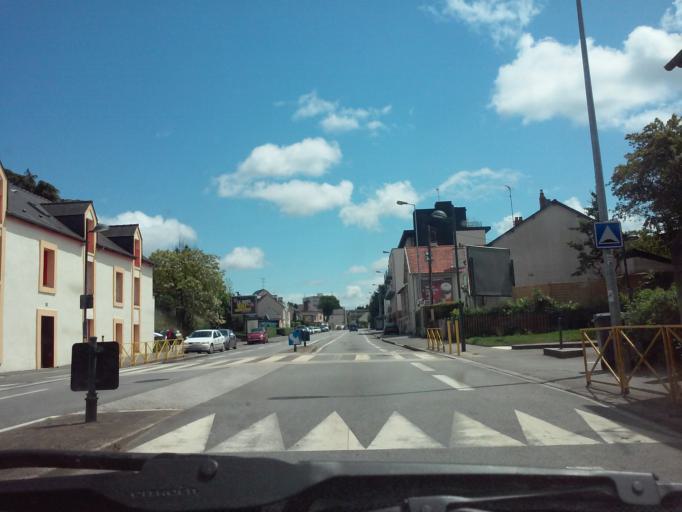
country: FR
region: Brittany
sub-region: Departement d'Ille-et-Vilaine
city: Rennes
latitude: 48.0997
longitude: -1.6476
